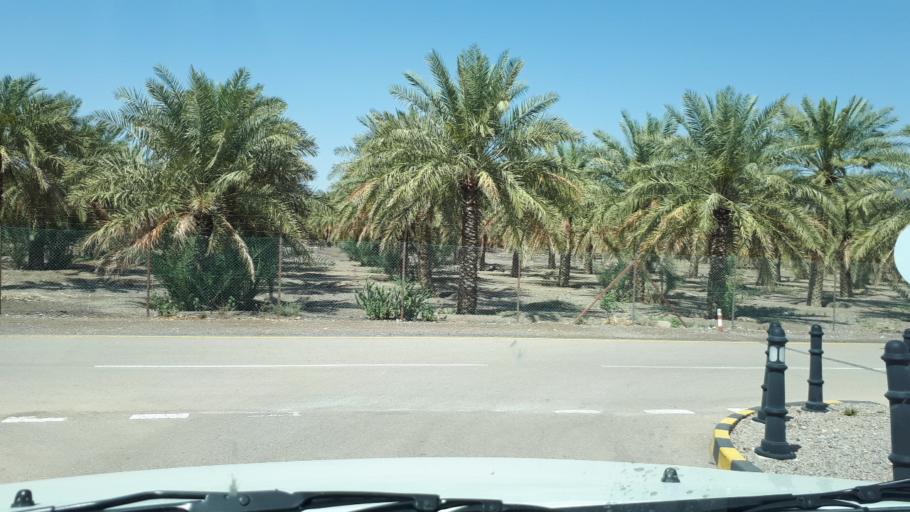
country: OM
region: Muhafazat ad Dakhiliyah
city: Bahla'
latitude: 22.9152
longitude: 57.2499
